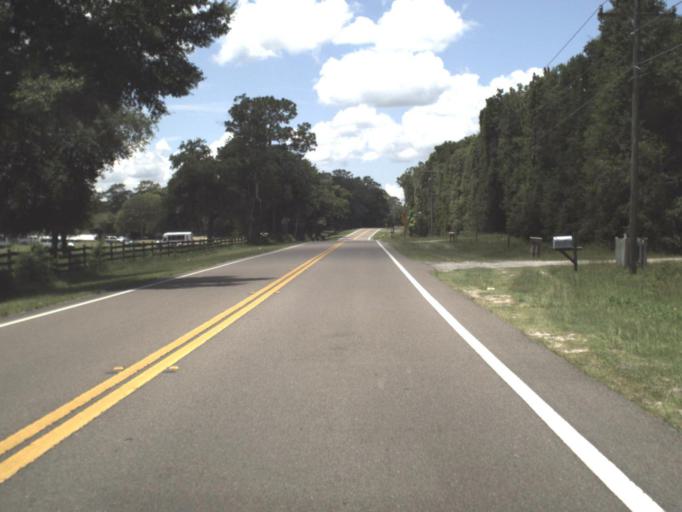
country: US
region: Florida
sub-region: Clay County
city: Keystone Heights
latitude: 29.7195
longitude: -82.0017
